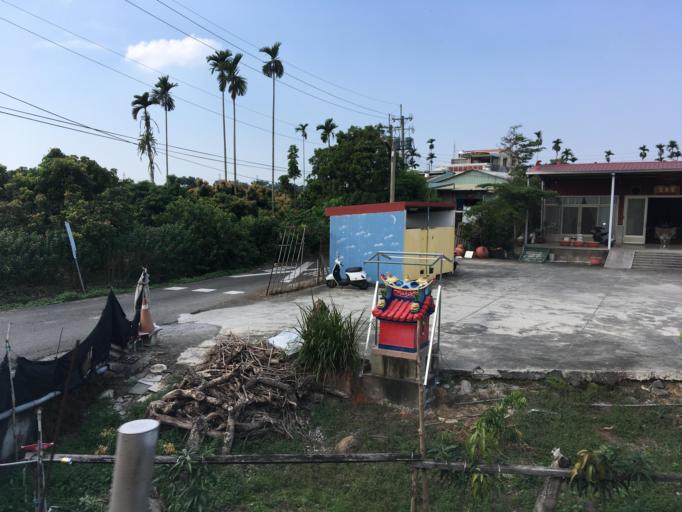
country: TW
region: Taiwan
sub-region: Chiayi
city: Jiayi Shi
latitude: 23.4926
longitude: 120.5210
